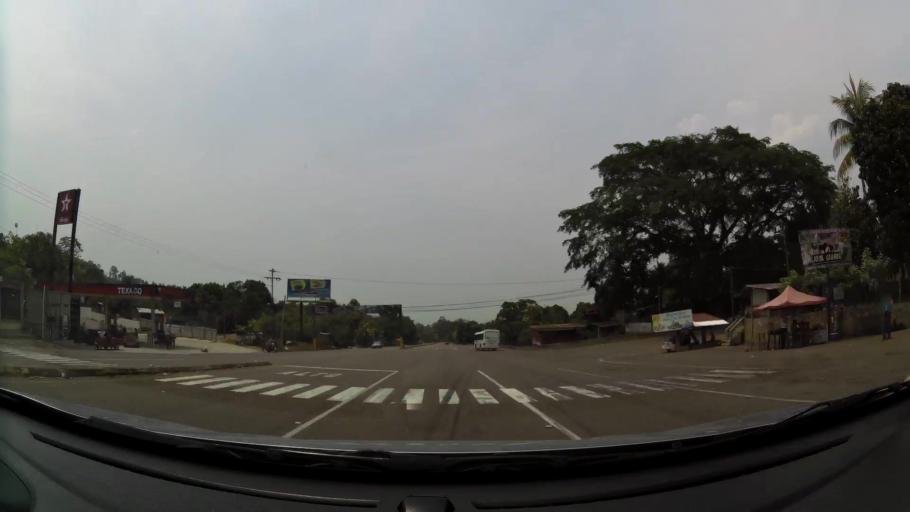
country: HN
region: Cortes
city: Santa Cruz de Yojoa
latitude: 14.9863
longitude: -87.9292
